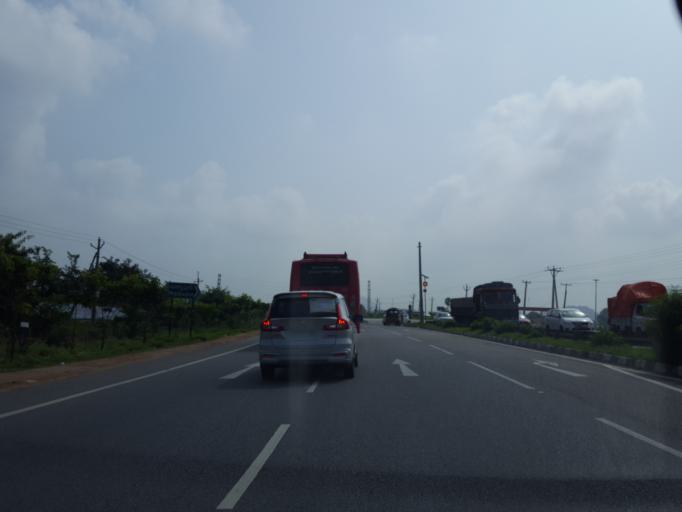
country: IN
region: Telangana
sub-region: Rangareddi
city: Ghatkesar
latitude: 17.2794
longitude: 78.7893
